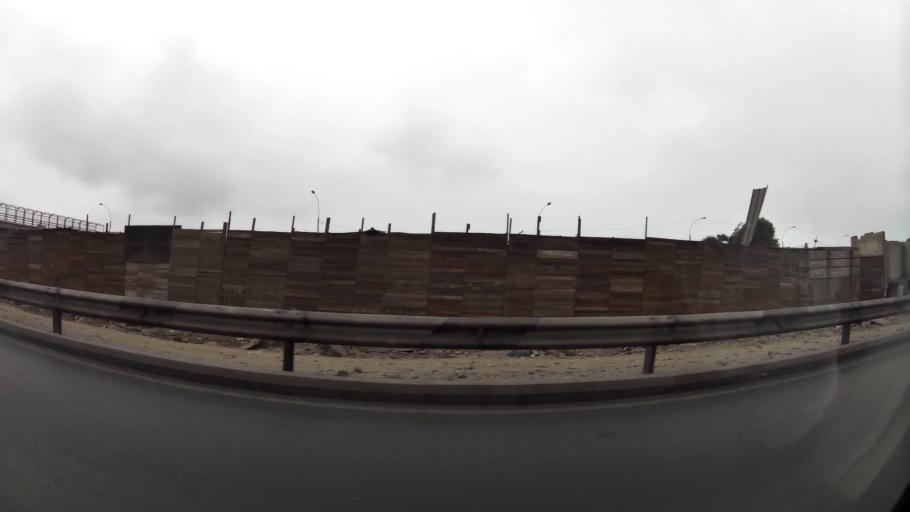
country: PE
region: Callao
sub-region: Callao
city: Callao
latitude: -12.0344
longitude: -77.1272
